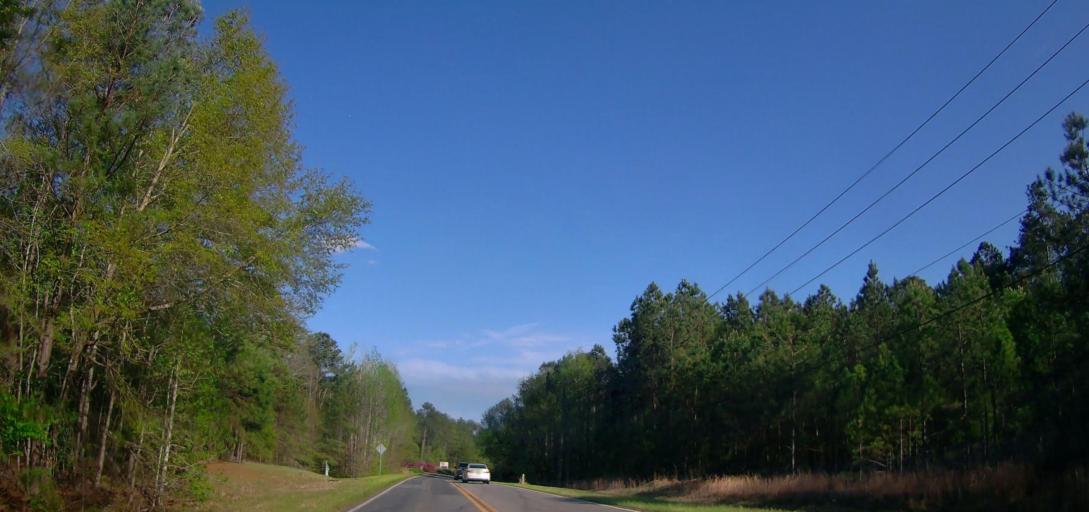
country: US
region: Georgia
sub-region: Baldwin County
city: Milledgeville
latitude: 33.1394
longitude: -83.2410
